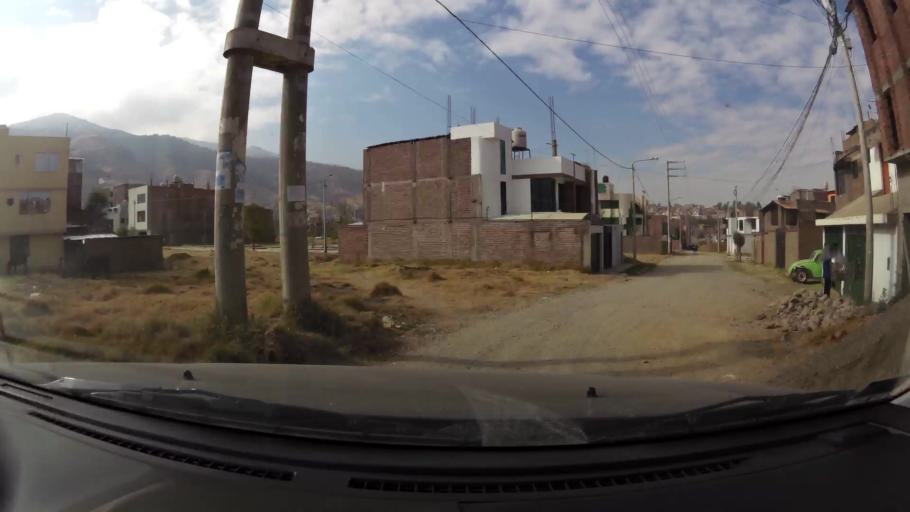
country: PE
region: Junin
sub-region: Provincia de Huancayo
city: Huancayo
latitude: -12.0507
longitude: -75.1929
